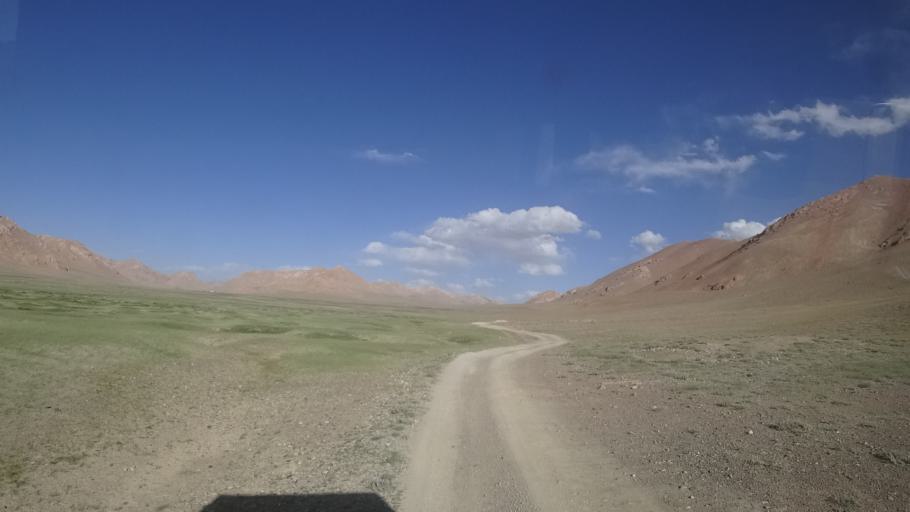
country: TJ
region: Gorno-Badakhshan
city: Murghob
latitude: 37.6569
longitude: 74.1648
